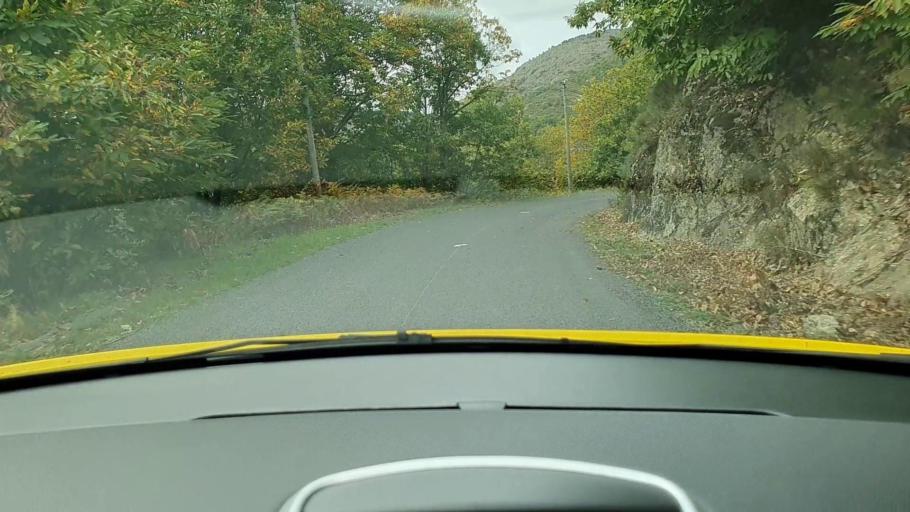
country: FR
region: Languedoc-Roussillon
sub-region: Departement de la Lozere
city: Meyrueis
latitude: 44.0607
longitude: 3.4273
